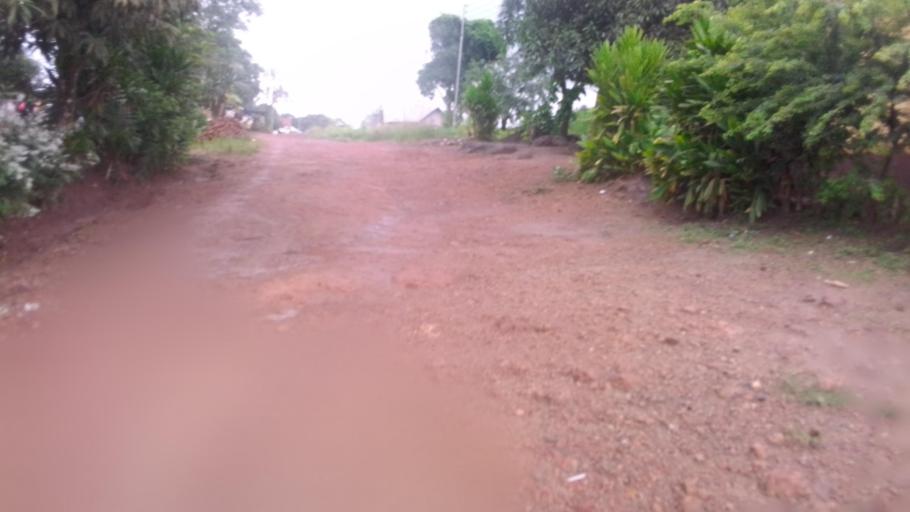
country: SL
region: Eastern Province
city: Kenema
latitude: 7.8880
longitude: -11.1746
